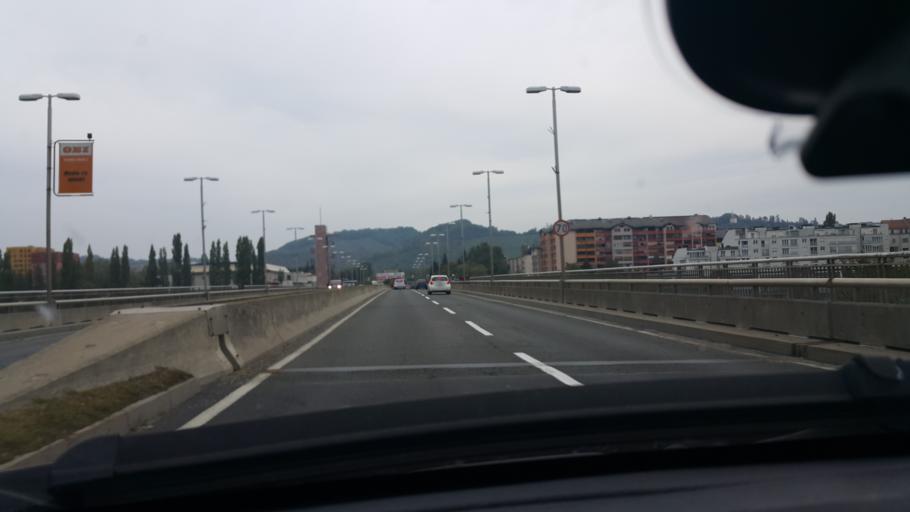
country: SI
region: Maribor
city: Kamnica
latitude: 46.5592
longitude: 15.6261
